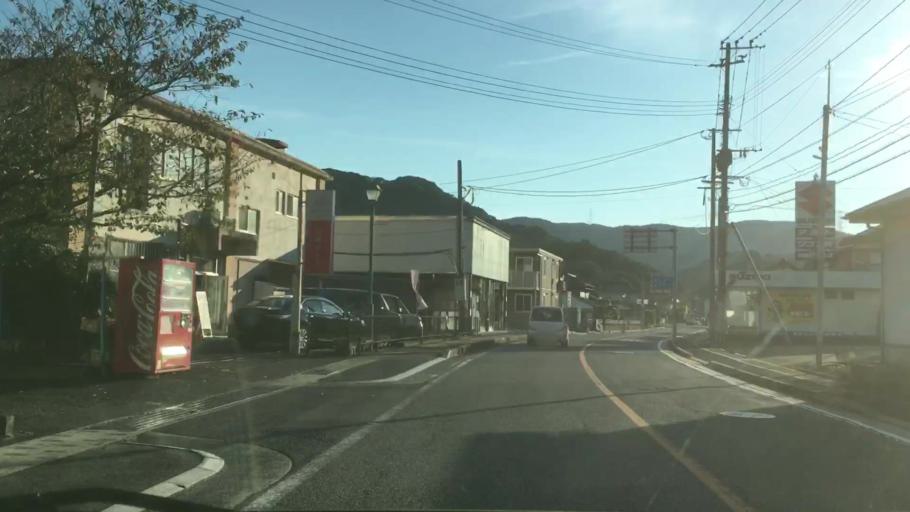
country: JP
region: Nagasaki
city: Sasebo
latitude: 33.0491
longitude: 129.7290
